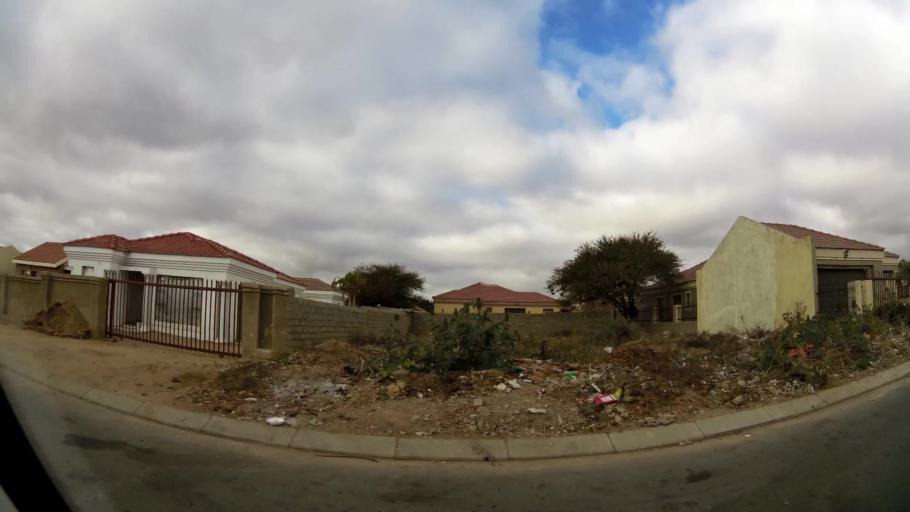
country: ZA
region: Limpopo
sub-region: Capricorn District Municipality
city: Polokwane
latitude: -23.9215
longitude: 29.4433
